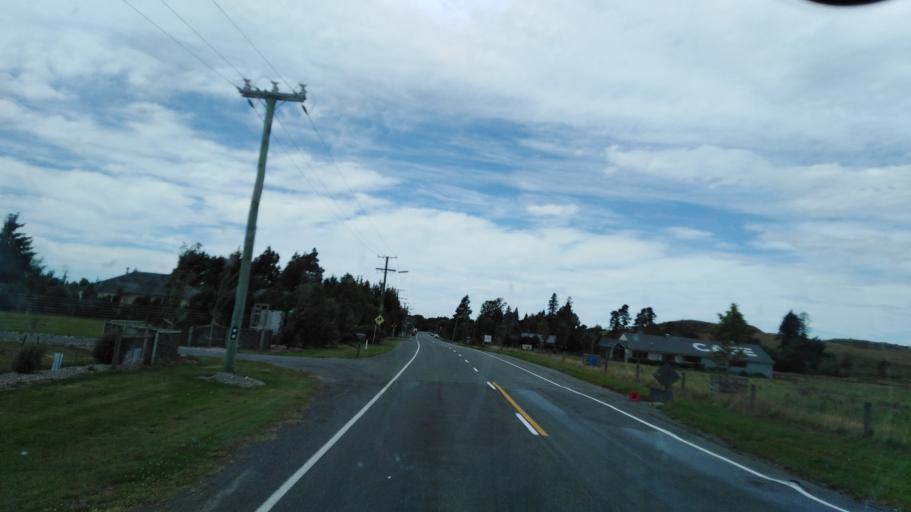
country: NZ
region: Canterbury
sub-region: Selwyn District
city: Darfield
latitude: -43.3362
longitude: 171.9232
